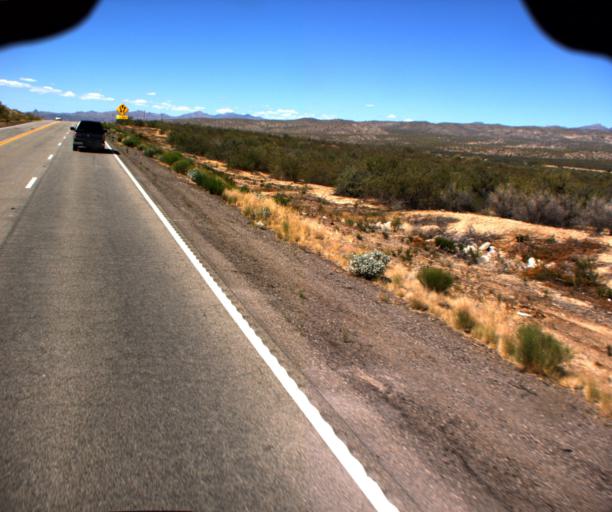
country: US
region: Arizona
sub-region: Yavapai County
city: Bagdad
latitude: 34.8066
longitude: -113.6259
